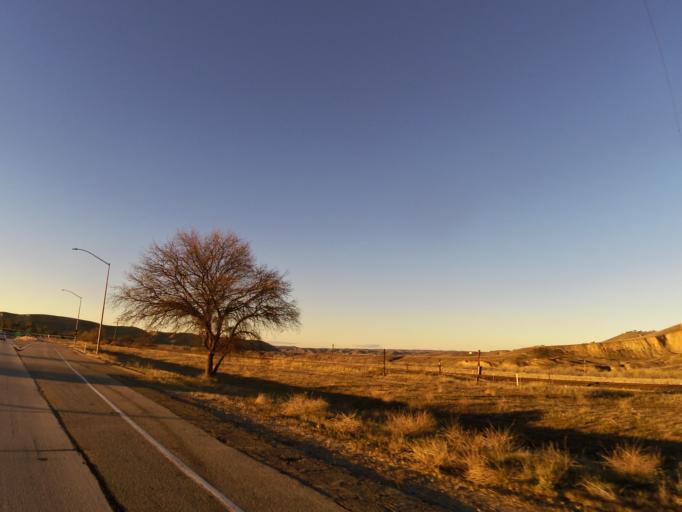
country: US
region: California
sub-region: San Luis Obispo County
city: San Miguel
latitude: 35.7965
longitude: -120.7384
